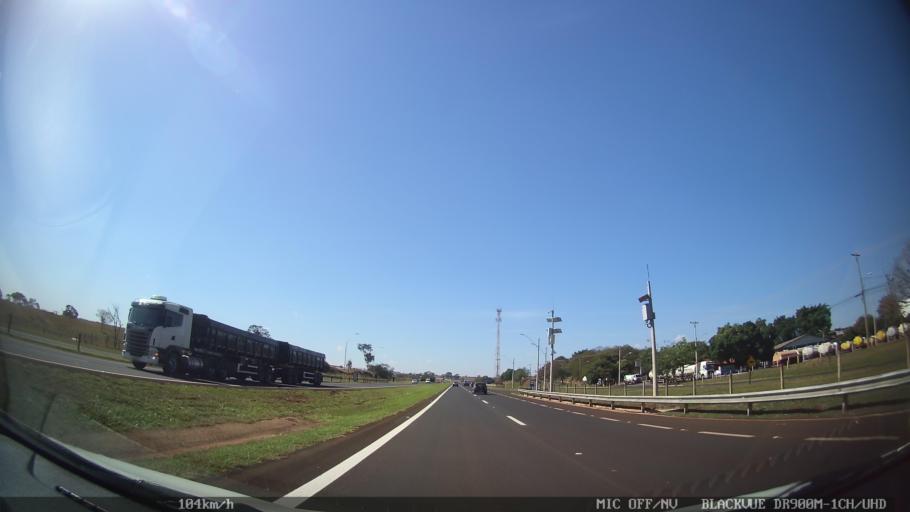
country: BR
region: Sao Paulo
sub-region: Ribeirao Preto
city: Ribeirao Preto
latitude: -21.1057
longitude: -47.8083
